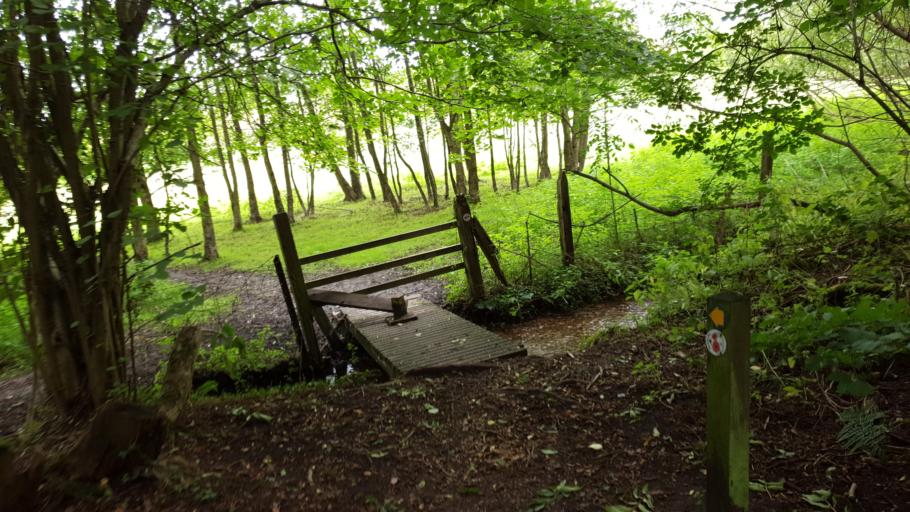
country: GB
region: England
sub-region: Suffolk
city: East Bergholt
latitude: 51.9418
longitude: 1.0159
